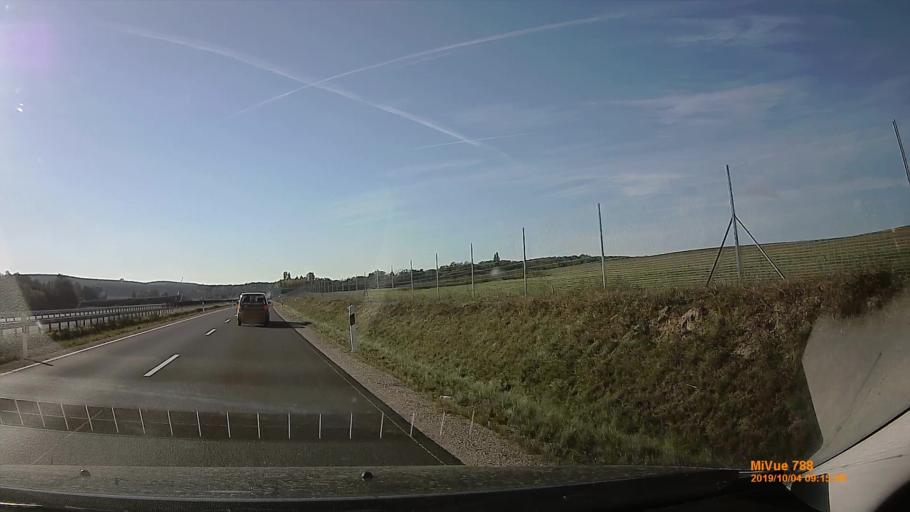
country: HU
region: Somogy
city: Karad
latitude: 46.6282
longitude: 17.7930
